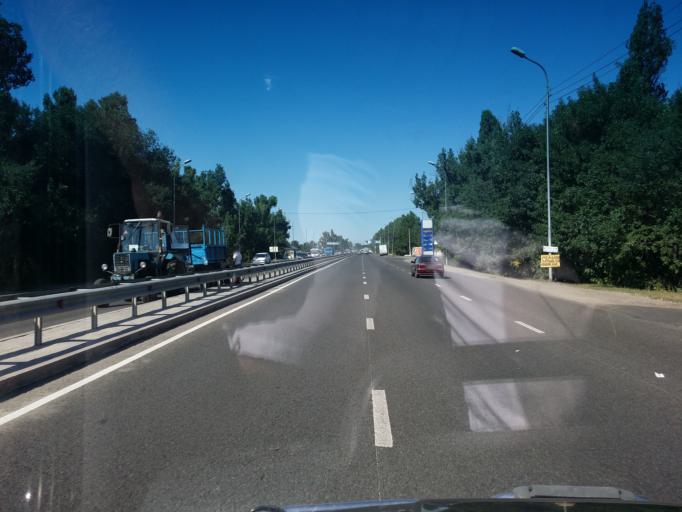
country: KZ
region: Almaty Qalasy
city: Almaty
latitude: 43.3137
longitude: 76.9015
